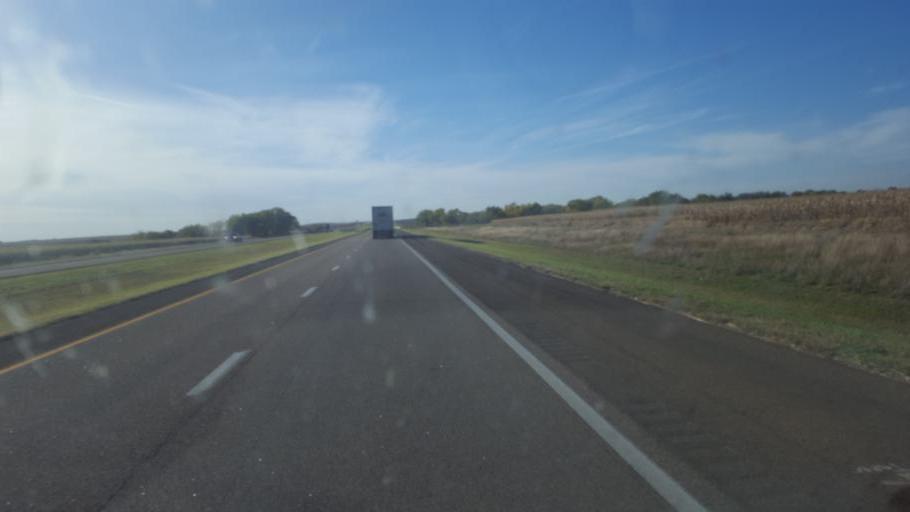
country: US
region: Kansas
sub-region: Ellis County
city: Ellis
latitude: 38.9701
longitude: -99.6596
